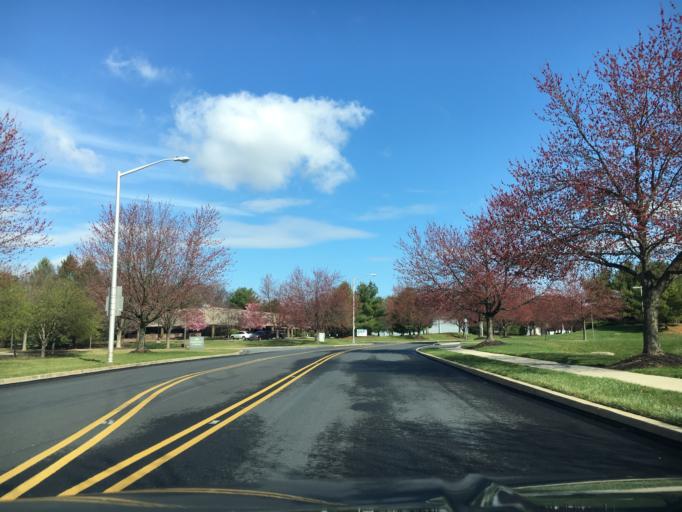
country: US
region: Pennsylvania
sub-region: Northampton County
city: Bethlehem
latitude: 40.6747
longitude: -75.3829
